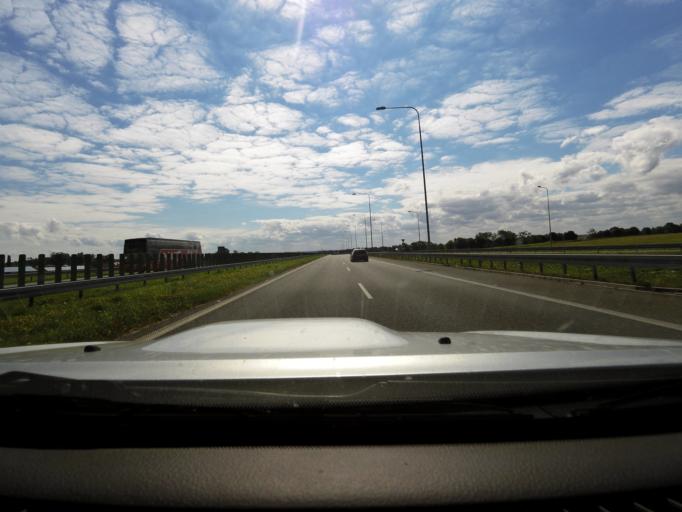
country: PL
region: Warmian-Masurian Voivodeship
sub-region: Powiat ostrodzki
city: Milomlyn
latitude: 53.7992
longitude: 19.7926
